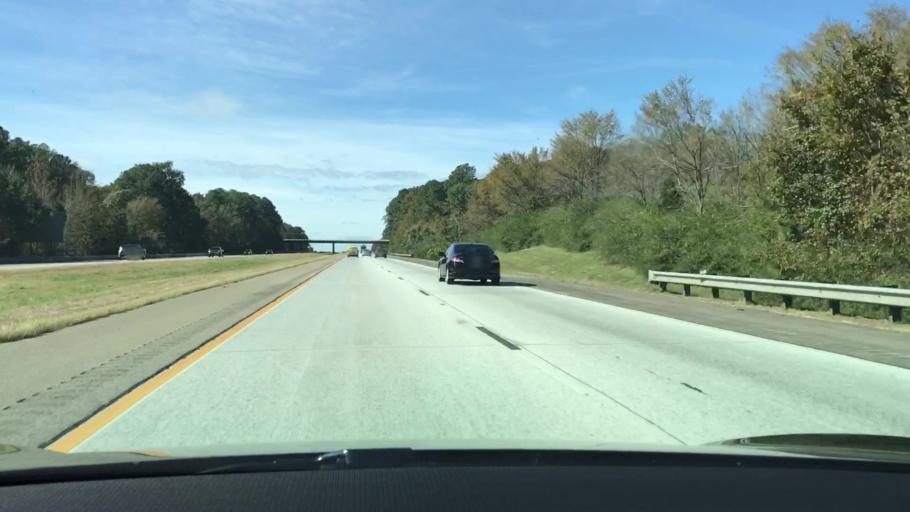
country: US
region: Georgia
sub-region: Greene County
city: Greensboro
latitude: 33.5401
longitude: -83.2310
